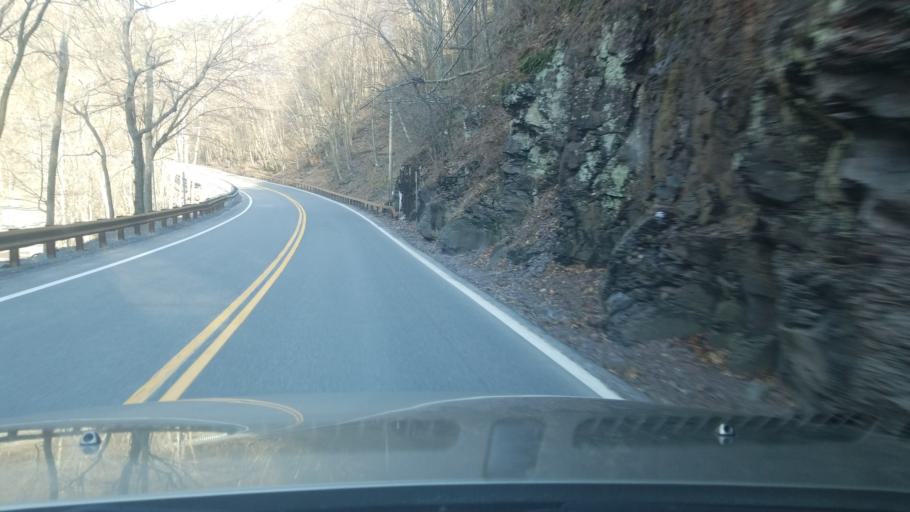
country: US
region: New York
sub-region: Greene County
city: Palenville
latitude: 42.1768
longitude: -74.0535
